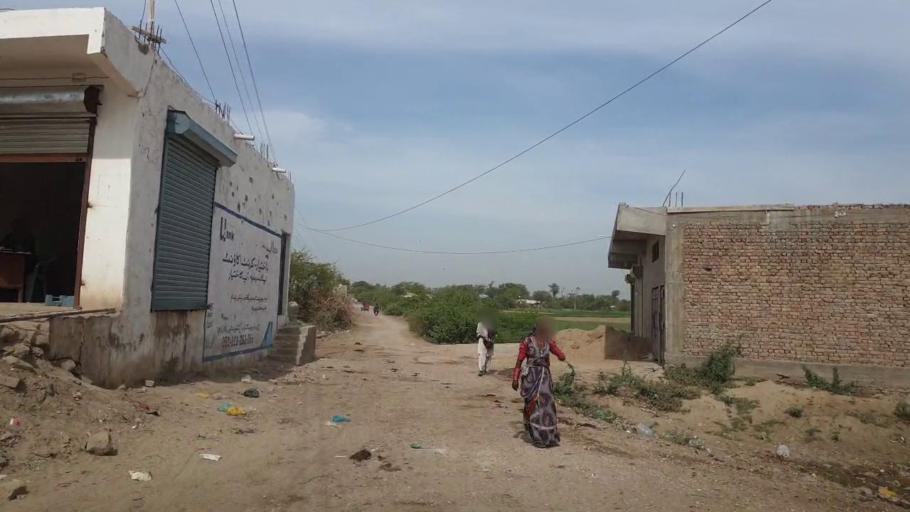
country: PK
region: Sindh
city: Kunri
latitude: 25.1777
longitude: 69.5815
